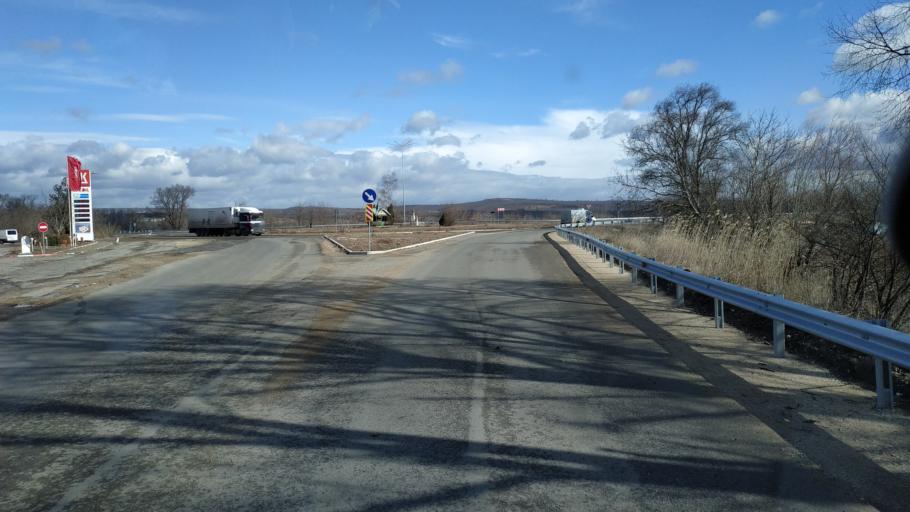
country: MD
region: Stinga Nistrului
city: Bucovat
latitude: 47.1797
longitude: 28.4662
